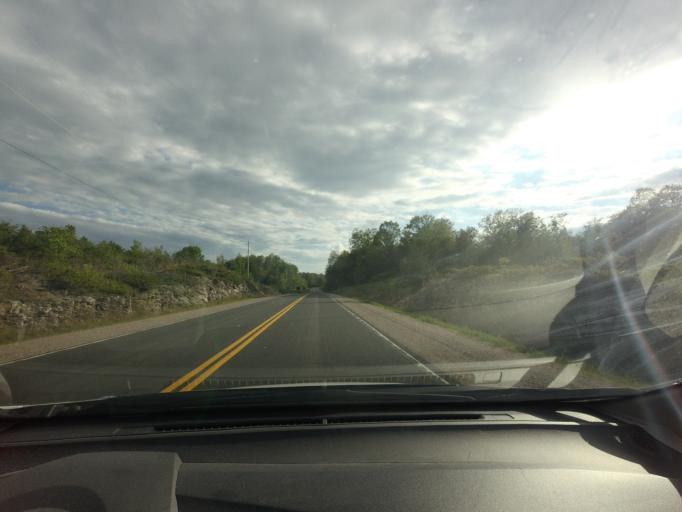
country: CA
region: Ontario
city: Perth
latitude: 44.7678
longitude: -76.3688
